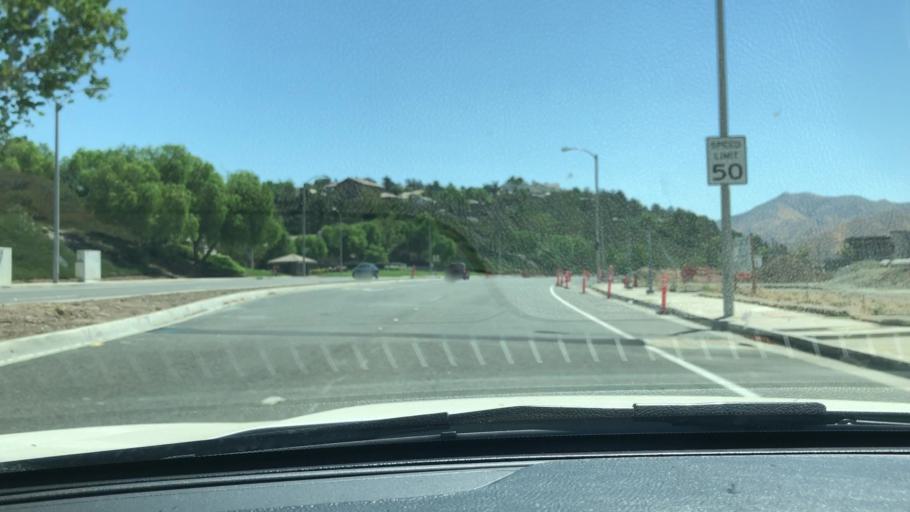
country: US
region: California
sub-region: Los Angeles County
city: Agua Dulce
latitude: 34.4354
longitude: -118.3908
